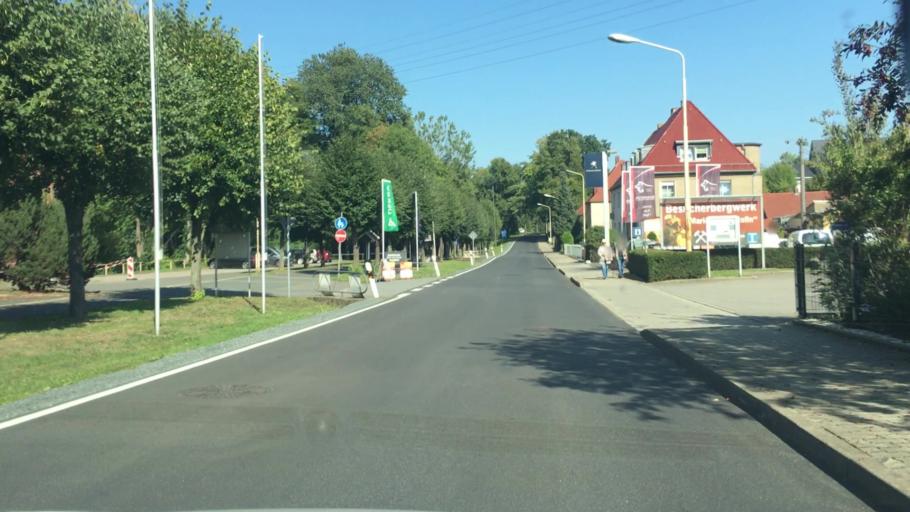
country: DE
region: Saxony
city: Dohma
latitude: 50.8752
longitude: 13.9488
